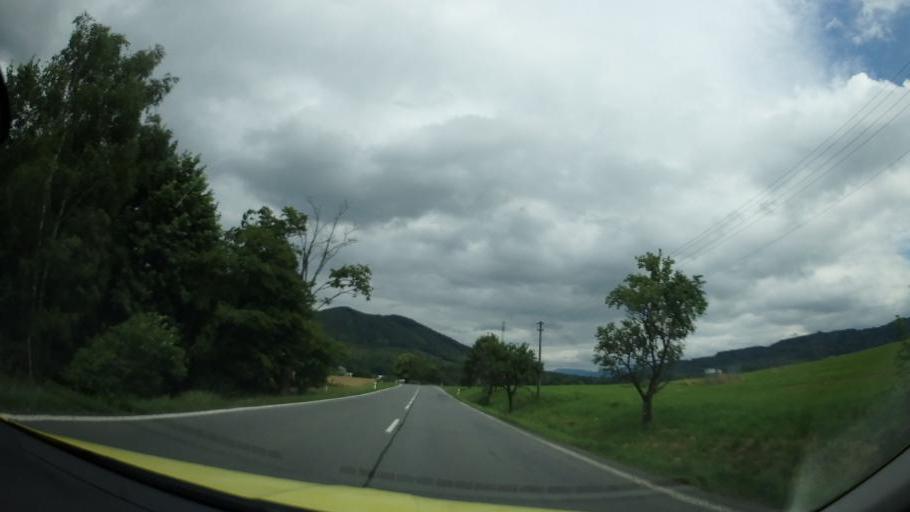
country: CZ
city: Stramberk
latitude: 49.5753
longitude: 18.1178
